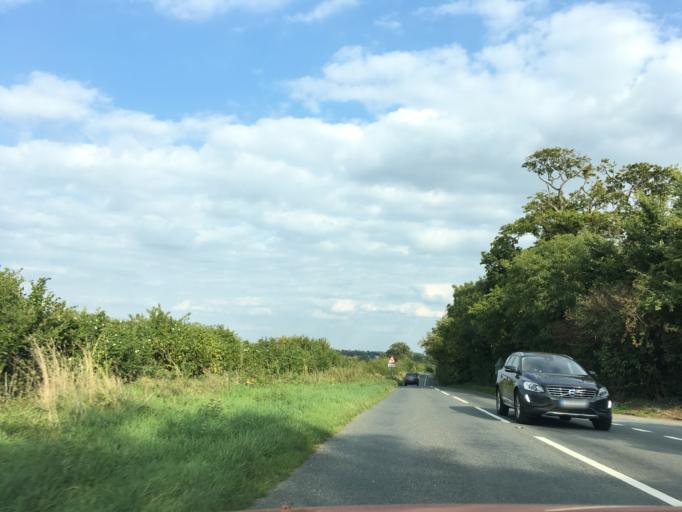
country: GB
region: England
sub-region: Gloucestershire
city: Tetbury
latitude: 51.6414
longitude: -2.1897
